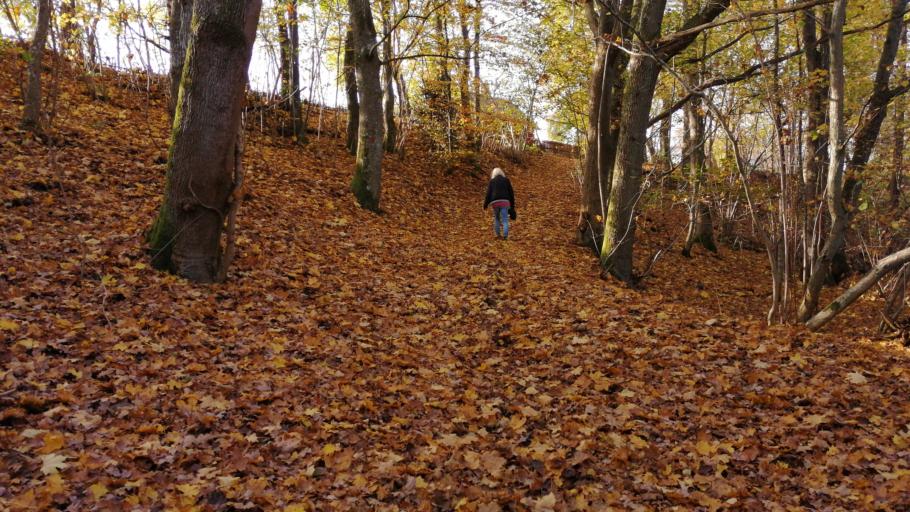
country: SE
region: Skane
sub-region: Klippans Kommun
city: Ljungbyhed
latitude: 56.0774
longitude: 13.2531
